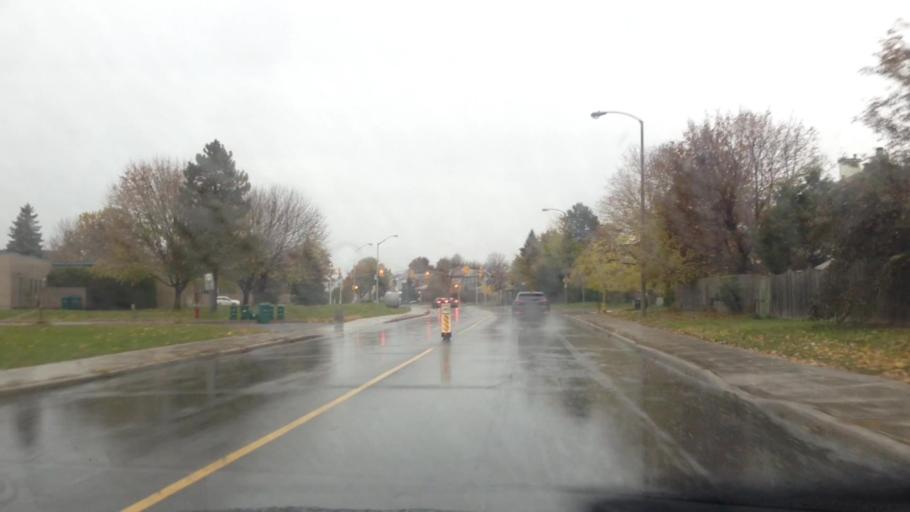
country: CA
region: Ontario
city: Clarence-Rockland
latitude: 45.4673
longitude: -75.4864
